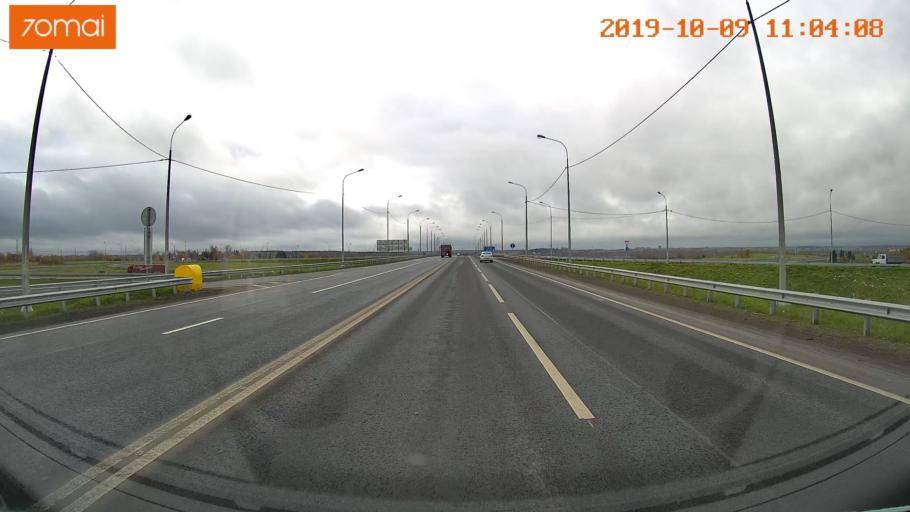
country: RU
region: Vologda
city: Vologda
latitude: 59.2153
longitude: 39.7707
